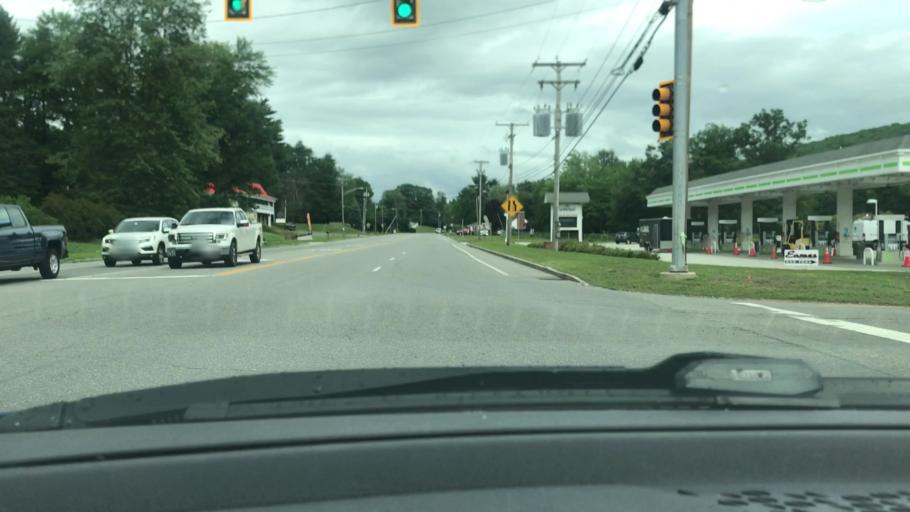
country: US
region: New Hampshire
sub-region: Merrimack County
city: Epsom
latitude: 43.2252
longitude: -71.3459
